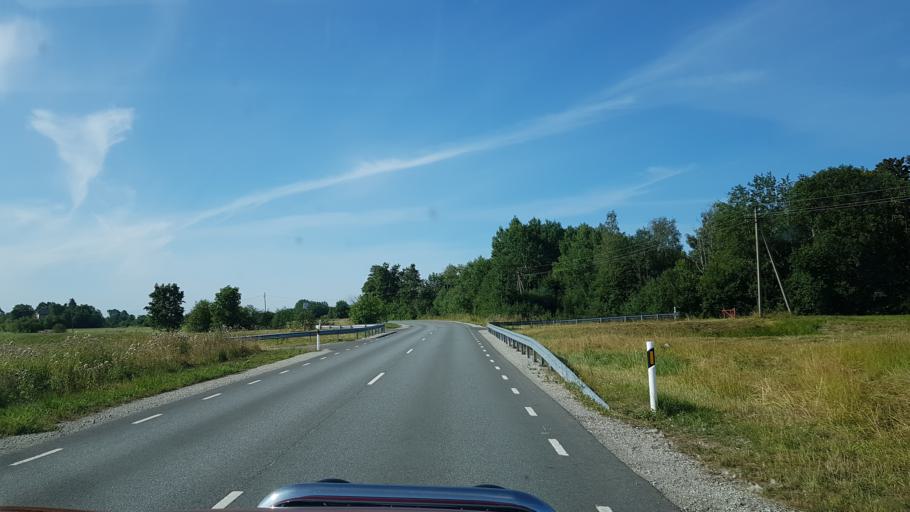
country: EE
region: Harju
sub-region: Rae vald
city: Jueri
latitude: 59.3771
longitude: 24.9273
